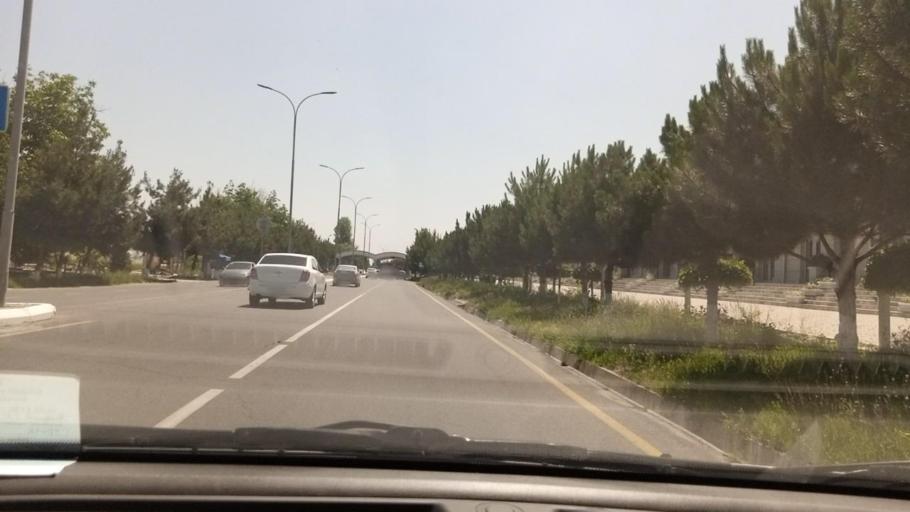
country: UZ
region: Toshkent
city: Urtaowul
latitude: 41.2169
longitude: 69.1739
